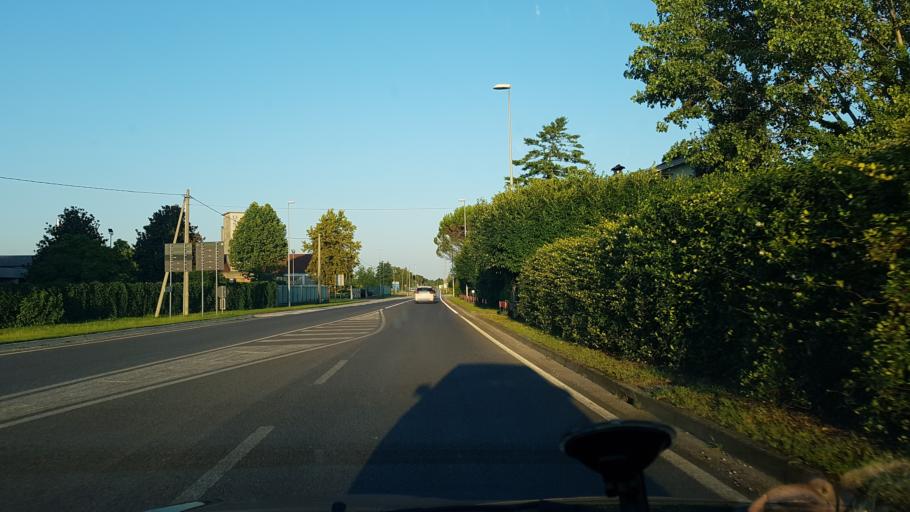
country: IT
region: Friuli Venezia Giulia
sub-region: Provincia di Udine
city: Martignacco
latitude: 46.0888
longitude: 13.1494
